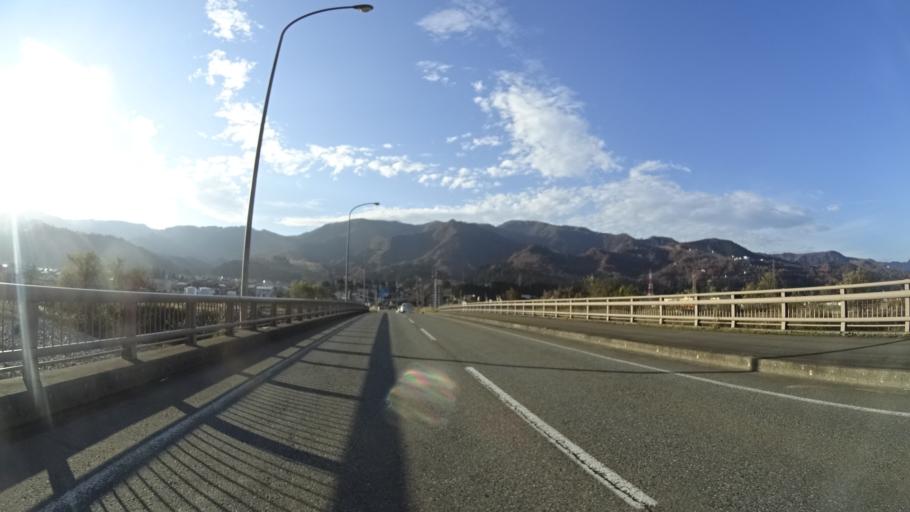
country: JP
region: Niigata
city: Shiozawa
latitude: 36.9890
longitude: 138.8134
